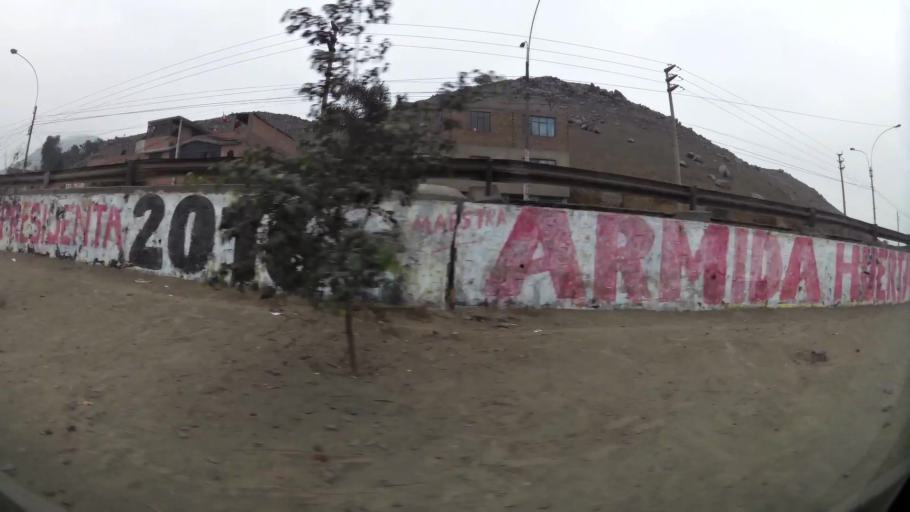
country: PE
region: Lima
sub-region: Lima
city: Urb. Santo Domingo
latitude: -11.9098
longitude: -77.0374
